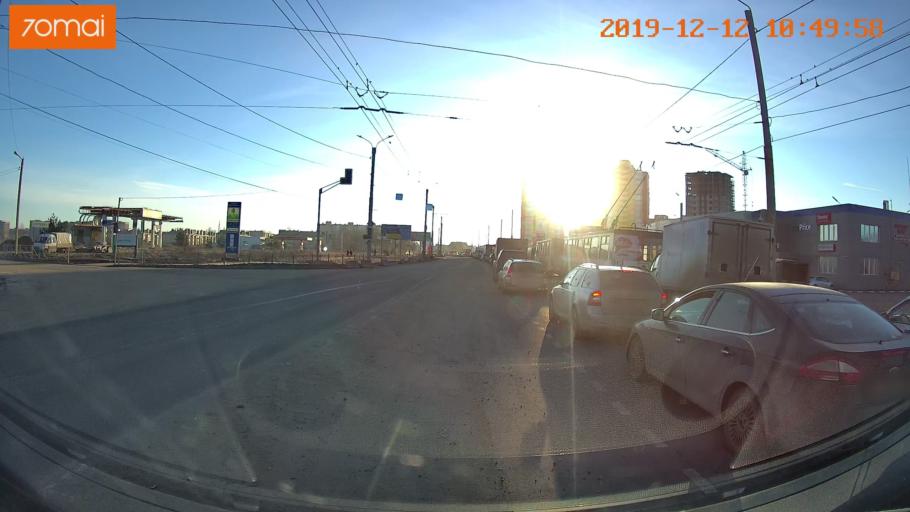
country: RU
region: Ivanovo
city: Kokhma
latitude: 56.9450
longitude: 41.0568
